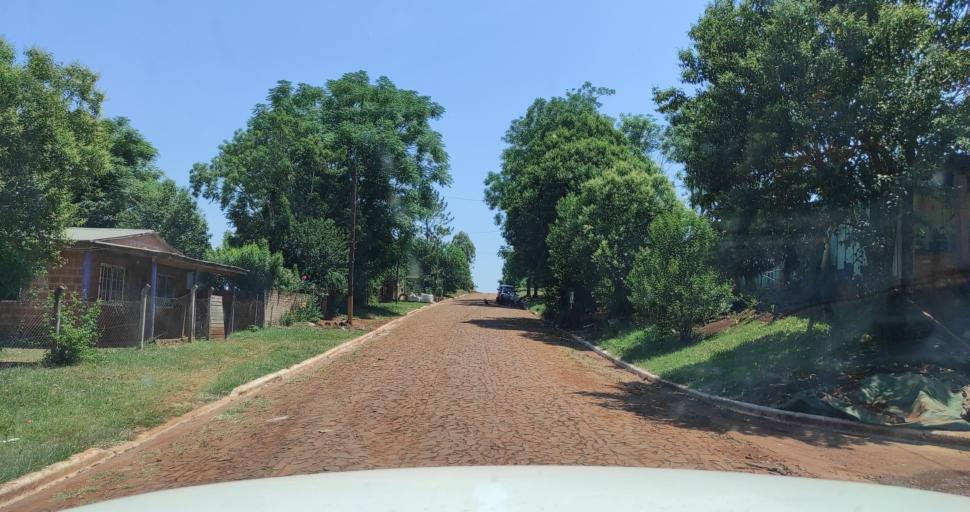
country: AR
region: Misiones
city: Santo Pipo
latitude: -27.1099
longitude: -55.3444
